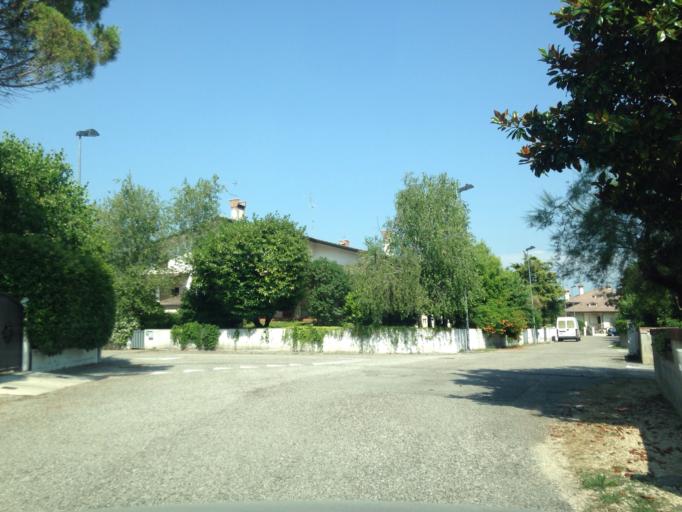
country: IT
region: Veneto
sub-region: Provincia di Venezia
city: Portogruaro
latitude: 45.7660
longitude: 12.8678
